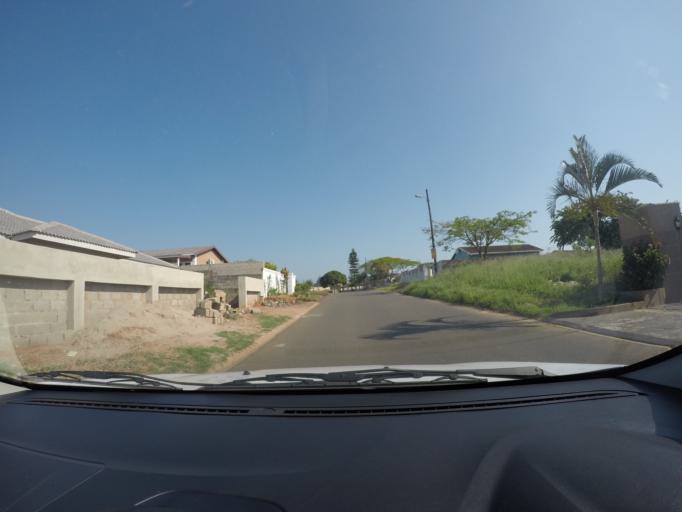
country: ZA
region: KwaZulu-Natal
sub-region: uThungulu District Municipality
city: Richards Bay
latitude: -28.7233
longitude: 32.0373
